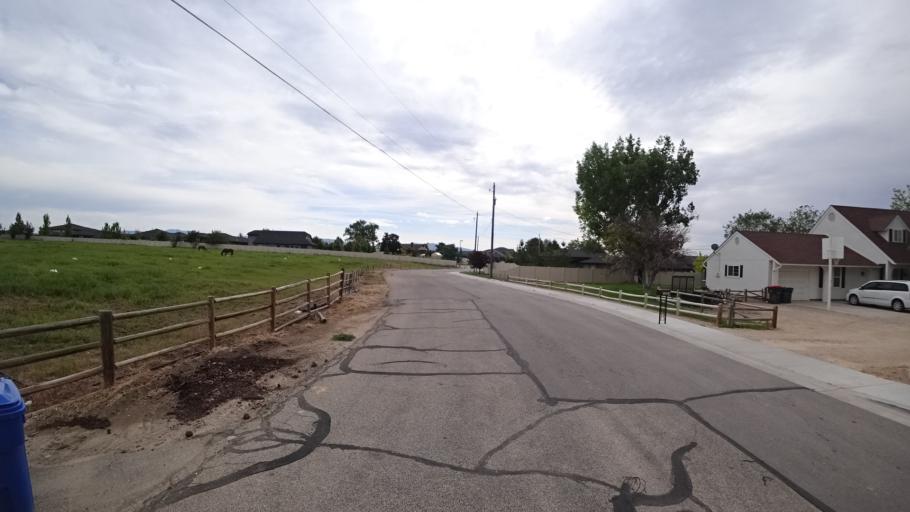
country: US
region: Idaho
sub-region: Ada County
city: Meridian
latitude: 43.5734
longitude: -116.3532
